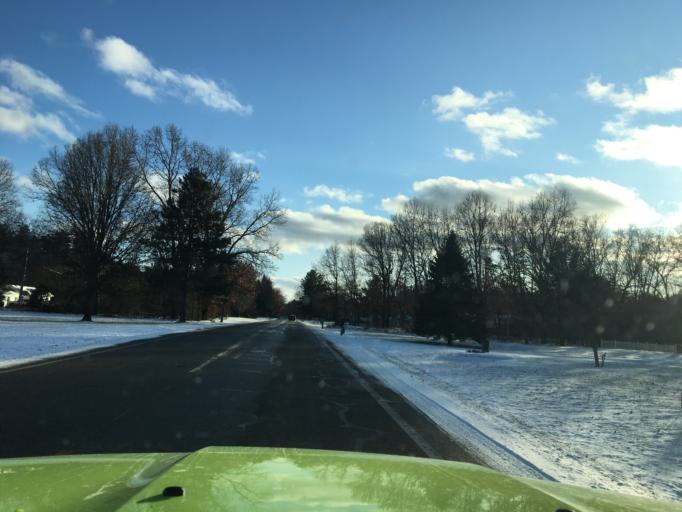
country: US
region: Michigan
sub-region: Montcalm County
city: Greenville
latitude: 43.2033
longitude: -85.2827
